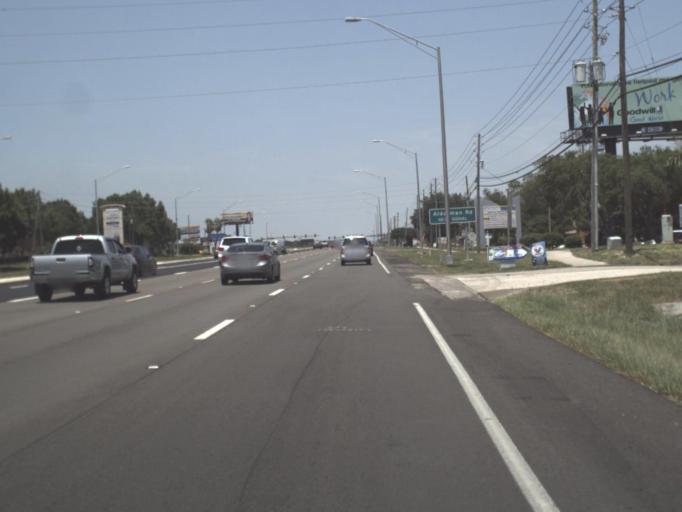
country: US
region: Florida
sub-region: Pinellas County
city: Palm Harbor
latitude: 28.0897
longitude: -82.7393
